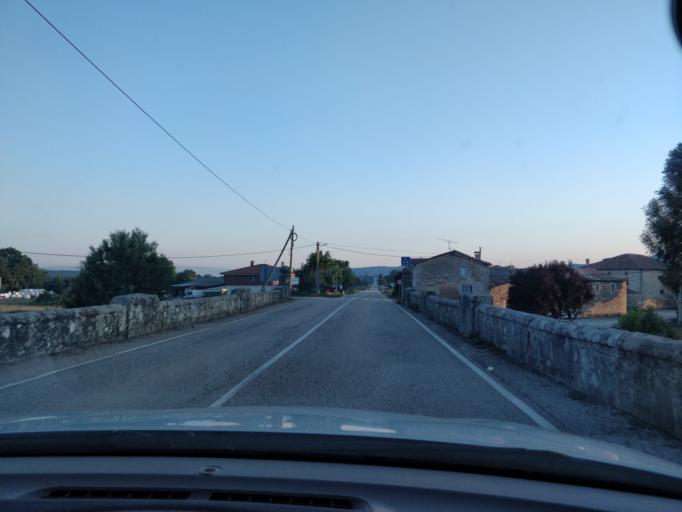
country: ES
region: Castille and Leon
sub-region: Provincia de Burgos
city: Espinosa de los Monteros
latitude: 43.0412
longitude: -3.4923
